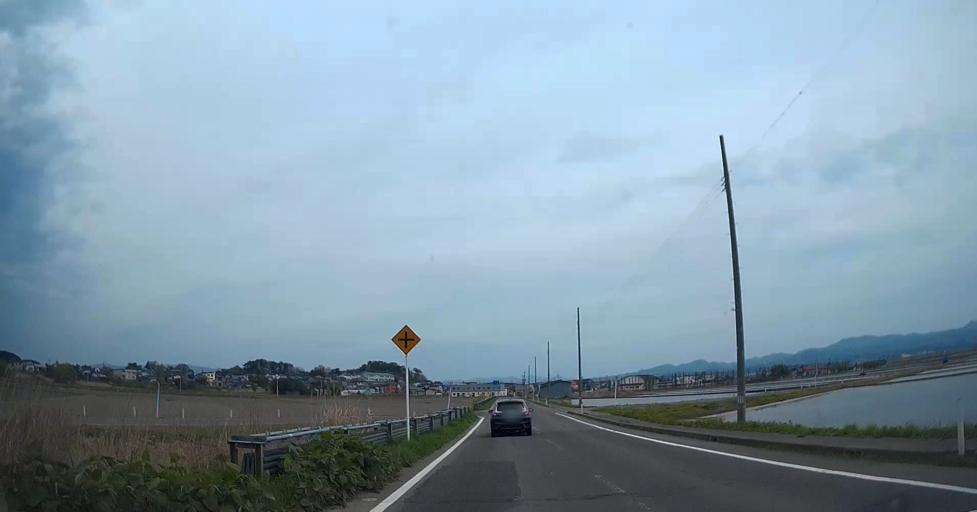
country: JP
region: Aomori
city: Shimokizukuri
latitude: 40.9751
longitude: 140.3684
